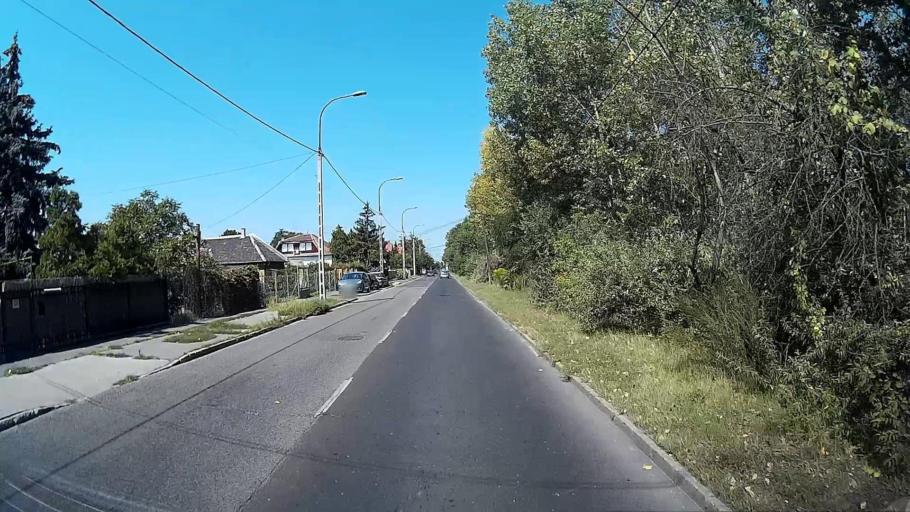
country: HU
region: Budapest
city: Budapest XXIII. keruelet
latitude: 47.4205
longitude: 19.1358
